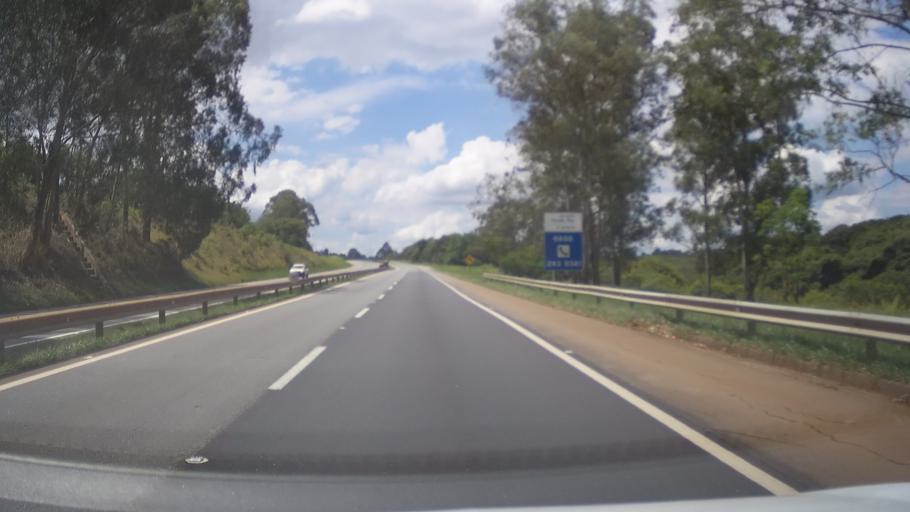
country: BR
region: Minas Gerais
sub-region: Nepomuceno
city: Nepomuceno
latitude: -21.2565
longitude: -45.1392
